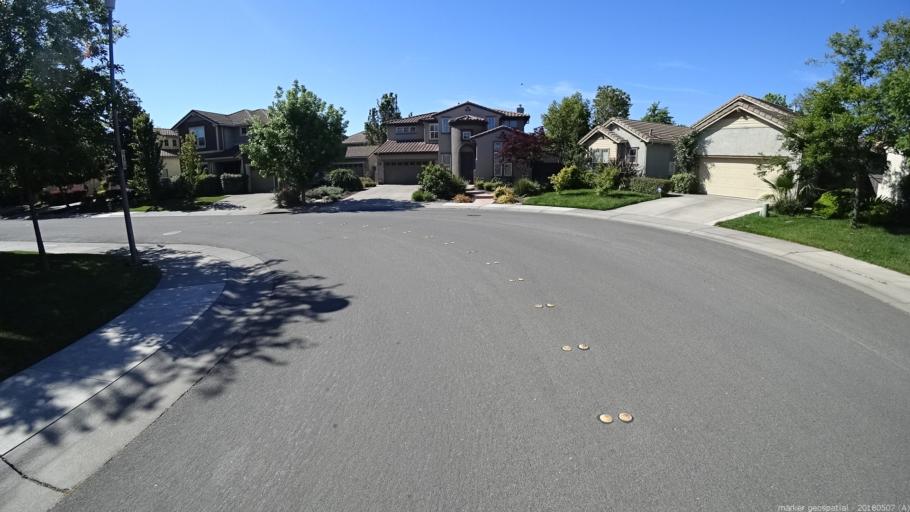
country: US
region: California
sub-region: Sacramento County
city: Rio Linda
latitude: 38.6650
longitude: -121.5033
